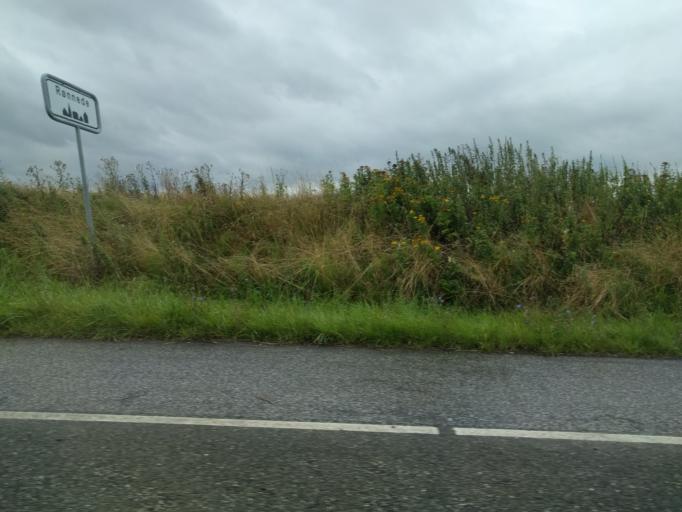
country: DK
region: Zealand
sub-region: Faxe Kommune
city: Ronnede
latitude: 55.2579
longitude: 12.0157
